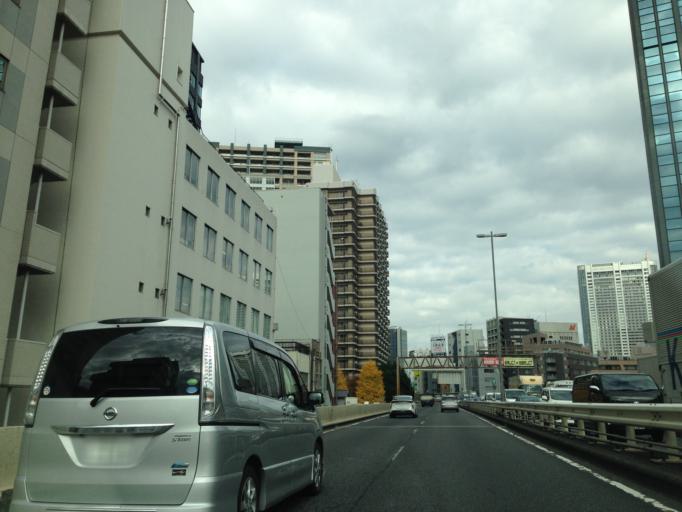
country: JP
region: Tokyo
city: Tokyo
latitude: 35.6970
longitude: 139.7525
